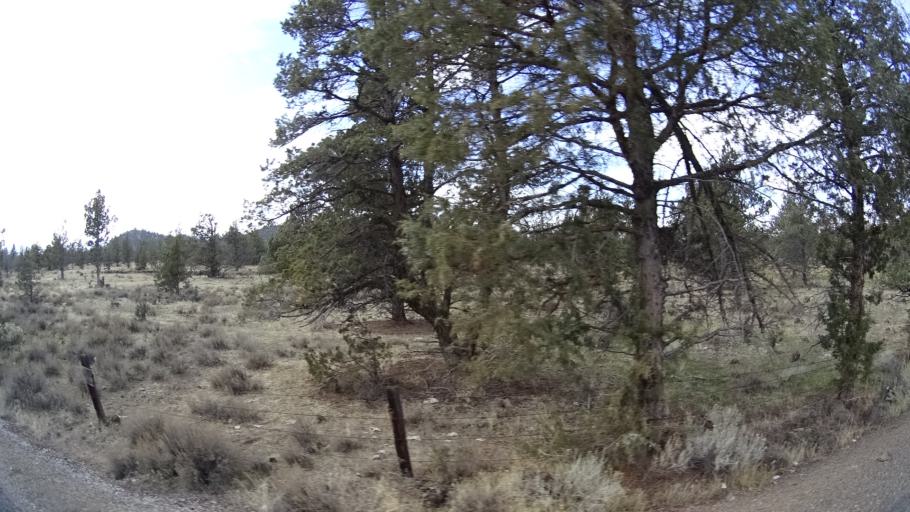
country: US
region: California
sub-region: Siskiyou County
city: Montague
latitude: 41.6370
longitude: -122.4383
